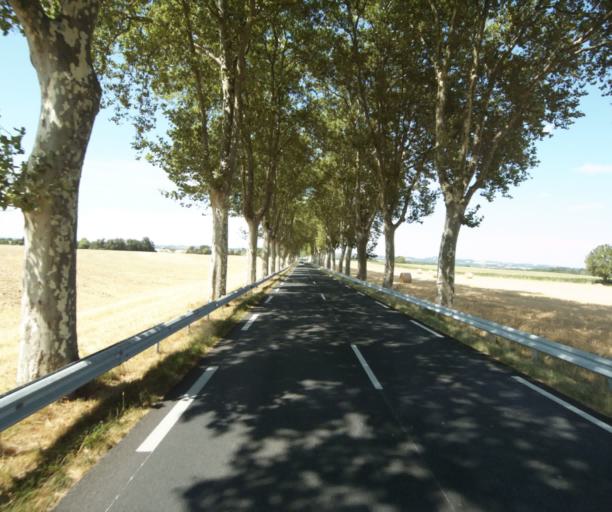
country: FR
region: Midi-Pyrenees
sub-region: Departement de la Haute-Garonne
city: Revel
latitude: 43.4909
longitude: 2.0132
